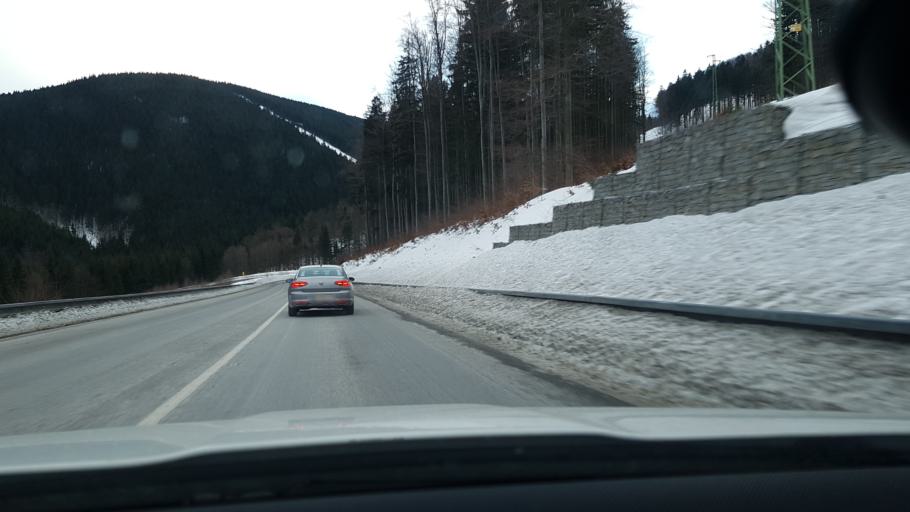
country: CZ
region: Olomoucky
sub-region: Okres Sumperk
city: Loucna nad Desnou
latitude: 50.1364
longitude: 17.1628
